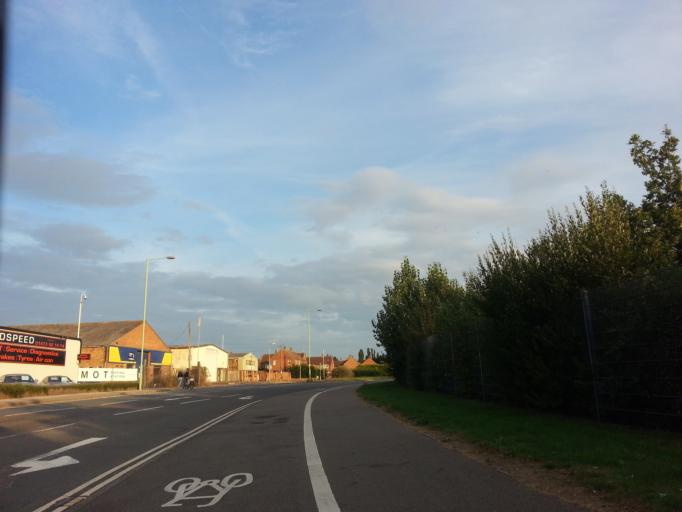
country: GB
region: England
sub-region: Suffolk
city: Bramford
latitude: 52.0460
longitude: 1.1070
